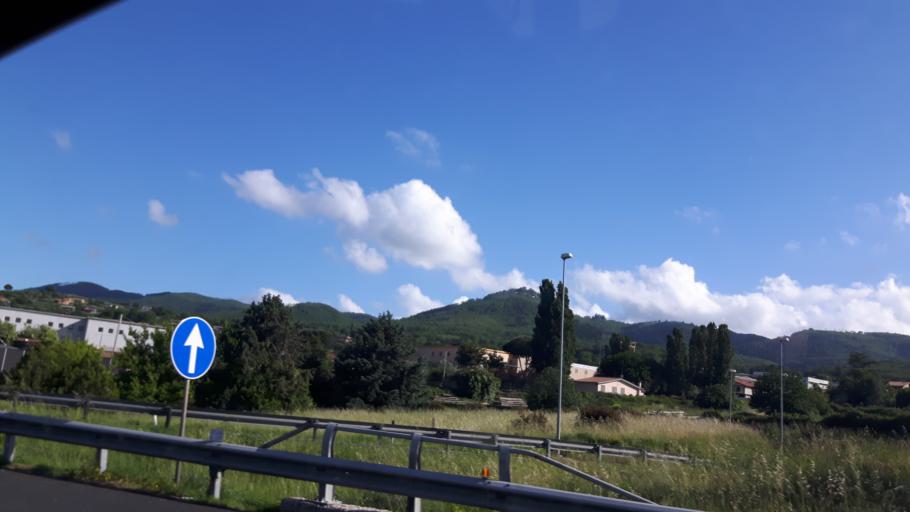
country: IT
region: Latium
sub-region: Citta metropolitana di Roma Capitale
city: Colonna
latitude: 41.8197
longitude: 12.7656
